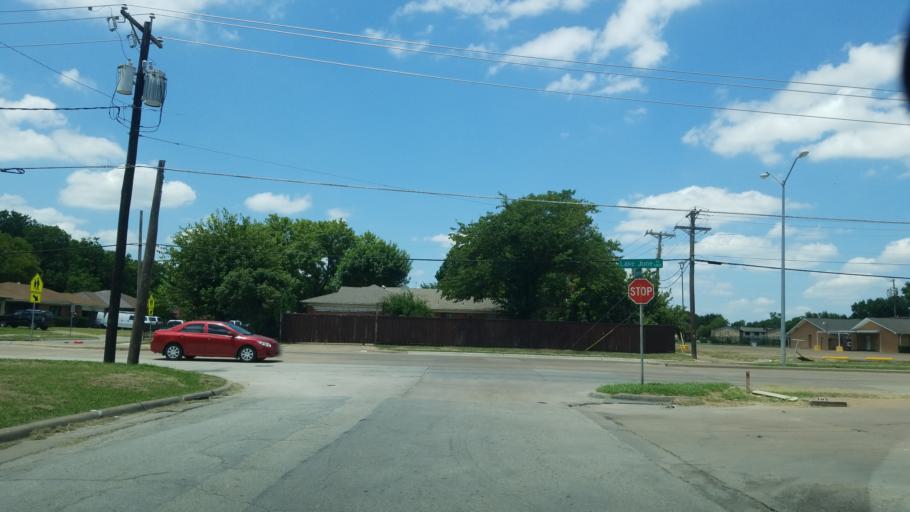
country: US
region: Texas
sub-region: Dallas County
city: Balch Springs
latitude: 32.7341
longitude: -96.7043
